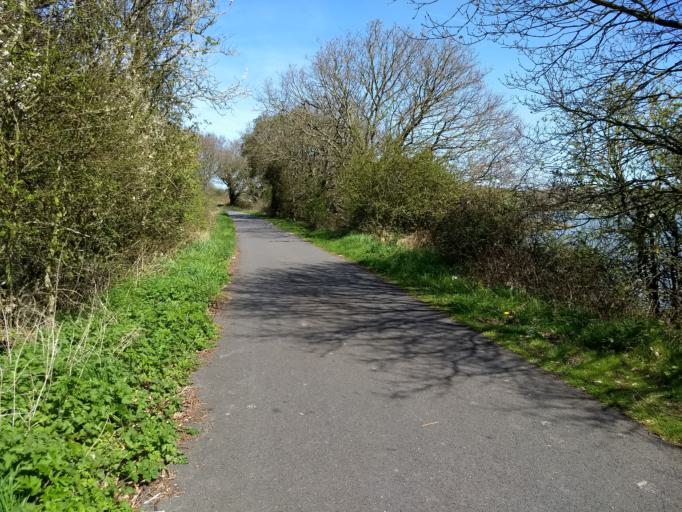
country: GB
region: England
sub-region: Isle of Wight
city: Newport
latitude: 50.7271
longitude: -1.2855
